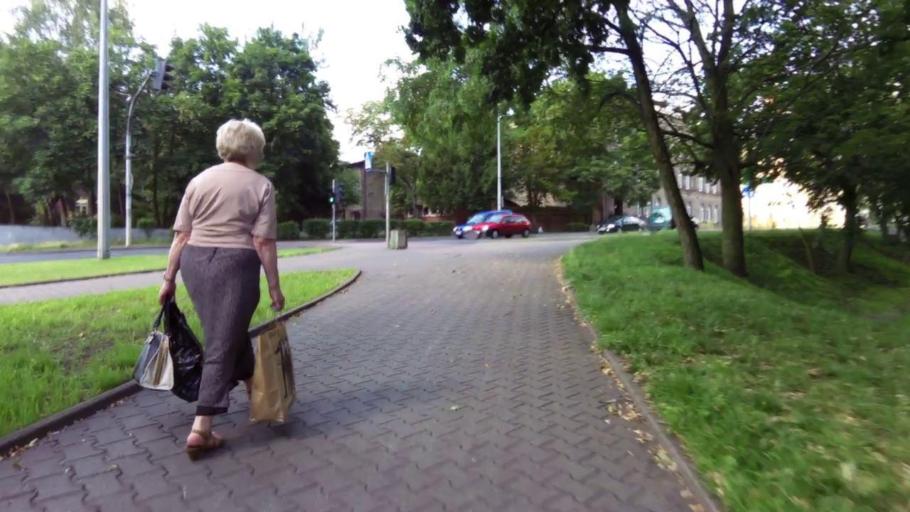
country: PL
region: West Pomeranian Voivodeship
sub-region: Powiat stargardzki
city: Stargard Szczecinski
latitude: 53.3345
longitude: 15.0427
